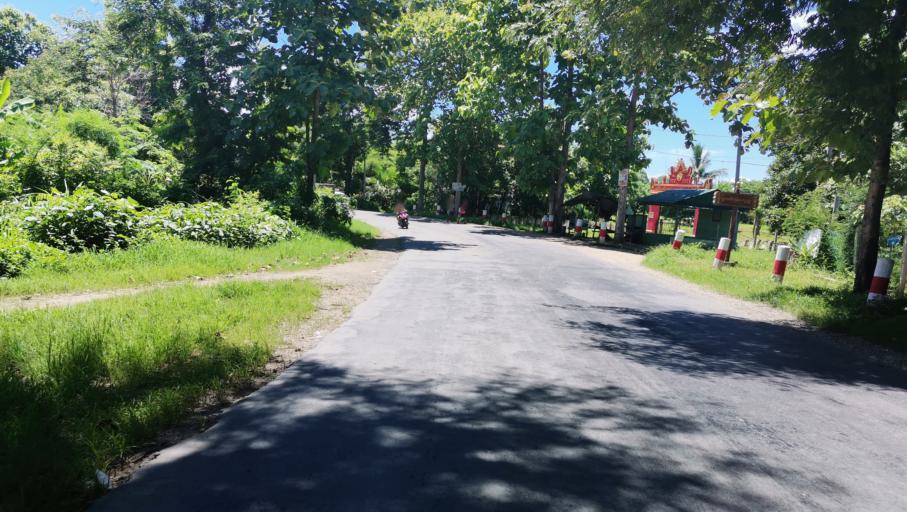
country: MM
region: Bago
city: Pyay
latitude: 18.8073
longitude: 95.1740
